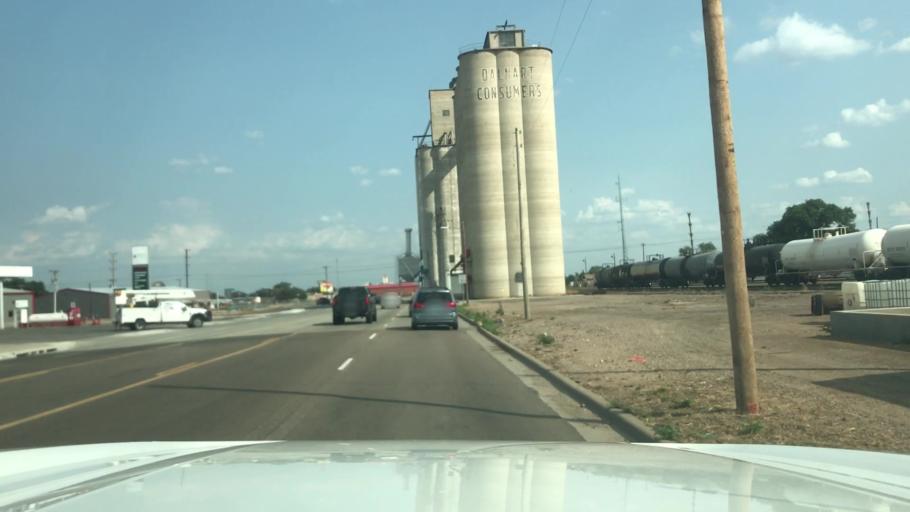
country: US
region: Texas
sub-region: Dallam County
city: Dalhart
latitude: 36.0684
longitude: -102.5265
